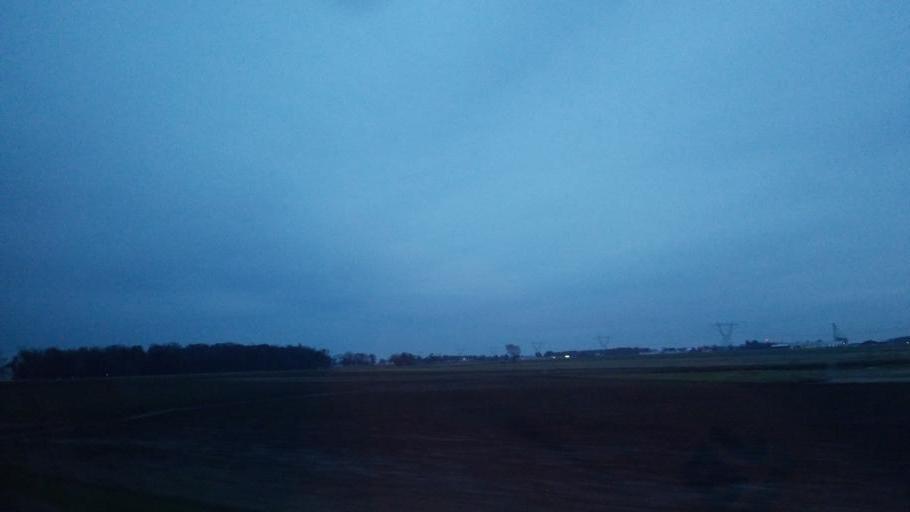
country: US
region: Indiana
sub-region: Adams County
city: Berne
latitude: 40.7158
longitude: -84.9723
